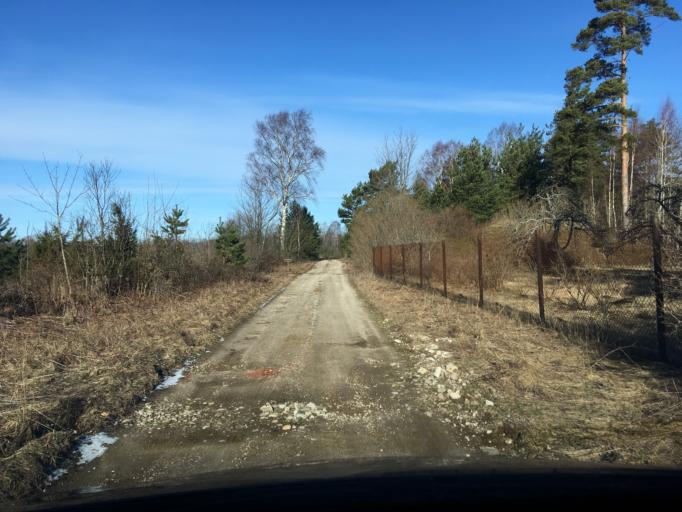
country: EE
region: Laeaene
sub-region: Lihula vald
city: Lihula
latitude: 58.5845
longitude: 23.7151
